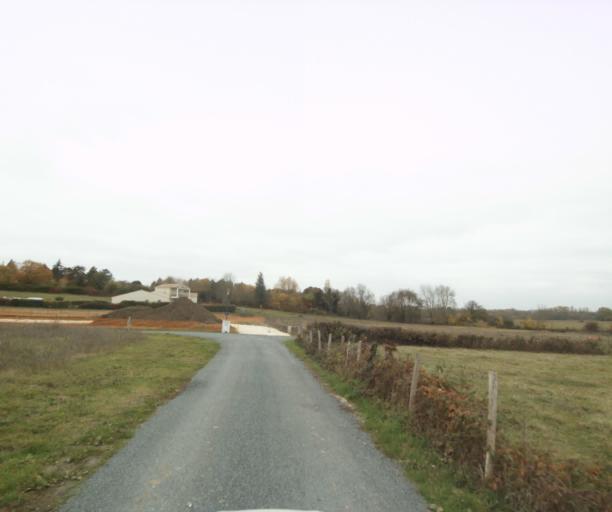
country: FR
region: Poitou-Charentes
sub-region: Departement de la Charente-Maritime
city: Les Gonds
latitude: 45.7223
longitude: -0.6306
